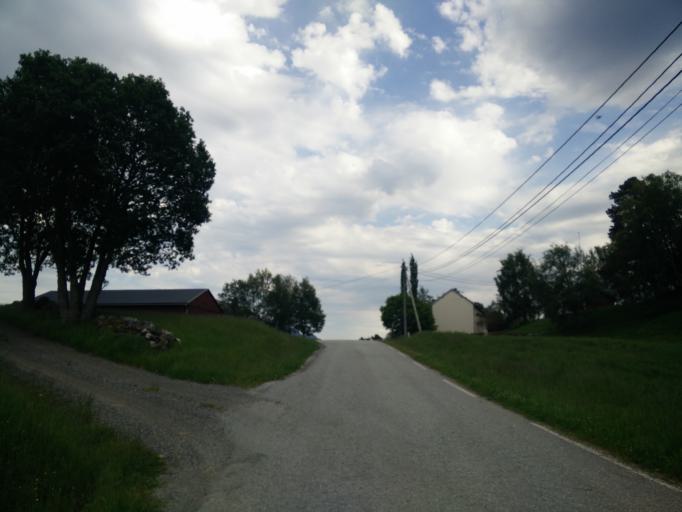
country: NO
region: More og Romsdal
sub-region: Kristiansund
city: Rensvik
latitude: 63.0372
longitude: 7.9532
